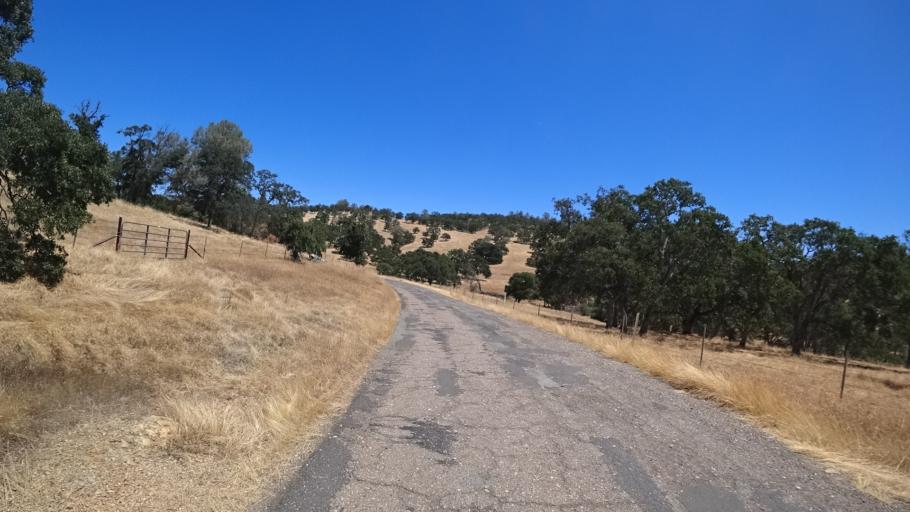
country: US
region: California
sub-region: Calaveras County
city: Rancho Calaveras
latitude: 38.0494
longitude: -120.7958
